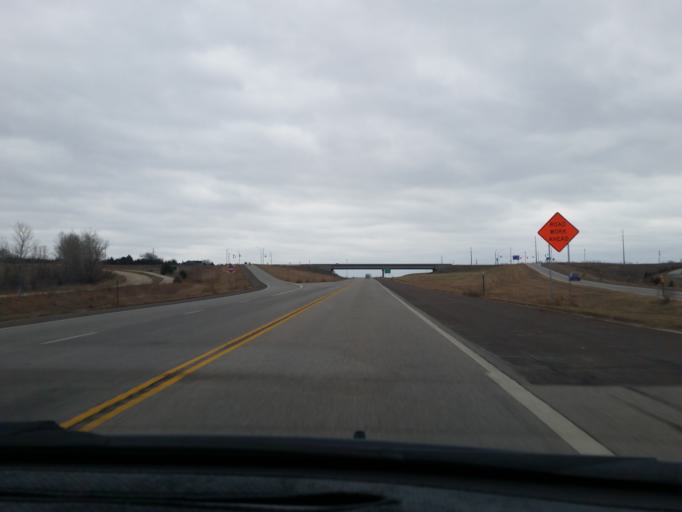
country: US
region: Kansas
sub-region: Douglas County
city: Lawrence
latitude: 38.9761
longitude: -95.3345
